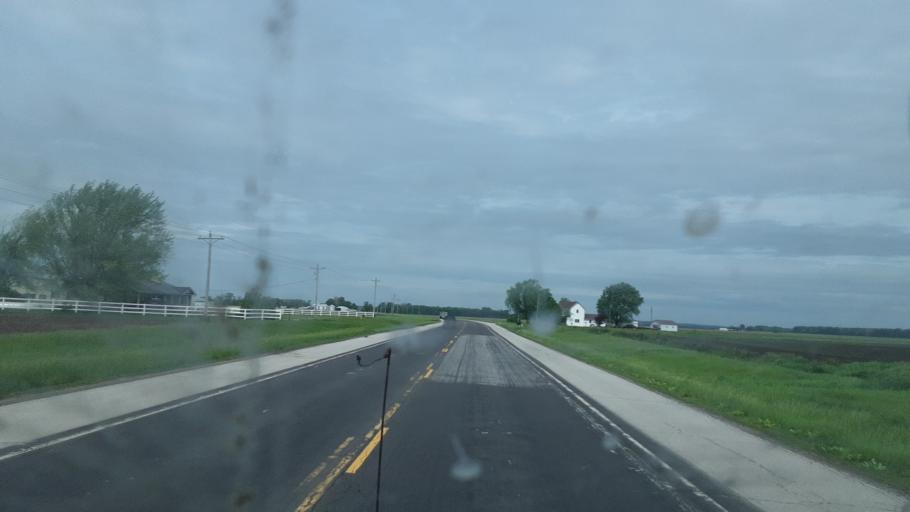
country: US
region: Illinois
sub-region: Hancock County
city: Warsaw
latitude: 40.3823
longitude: -91.5012
